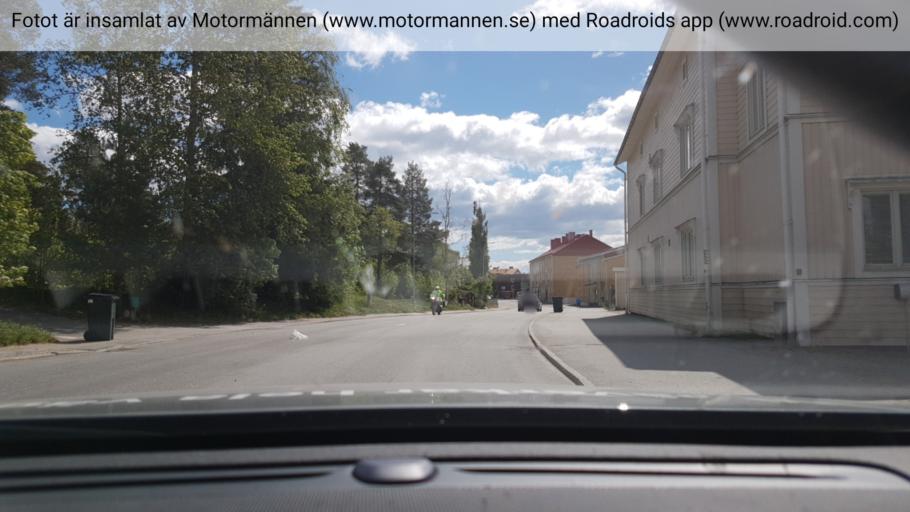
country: SE
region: Vaesterbotten
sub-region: Nordmalings Kommun
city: Nordmaling
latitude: 63.5721
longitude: 19.4953
